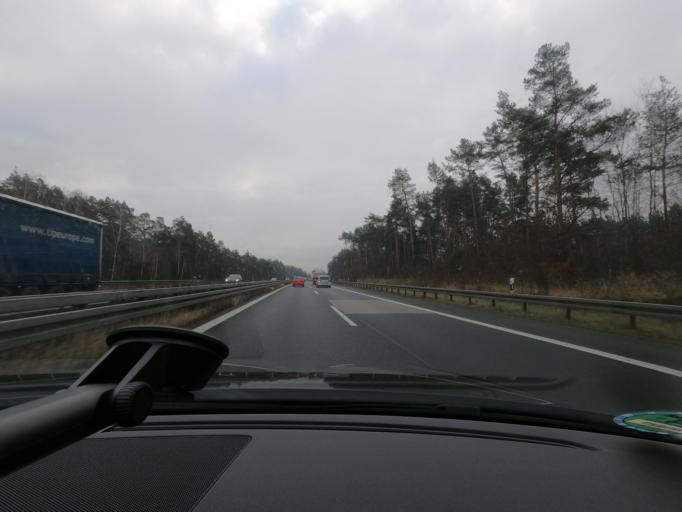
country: DE
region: Bavaria
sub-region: Upper Franconia
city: Gundelsheim
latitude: 49.9184
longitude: 10.9326
